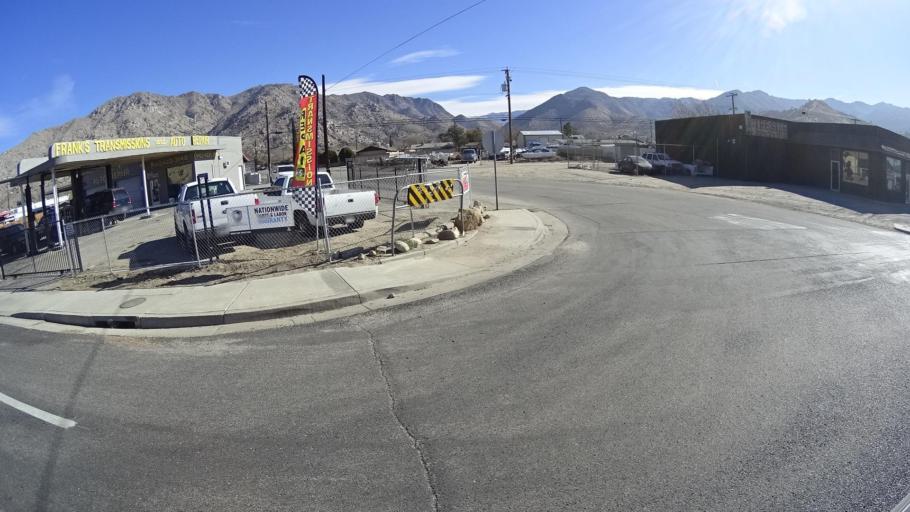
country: US
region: California
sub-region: Kern County
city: Lake Isabella
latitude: 35.6128
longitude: -118.4812
